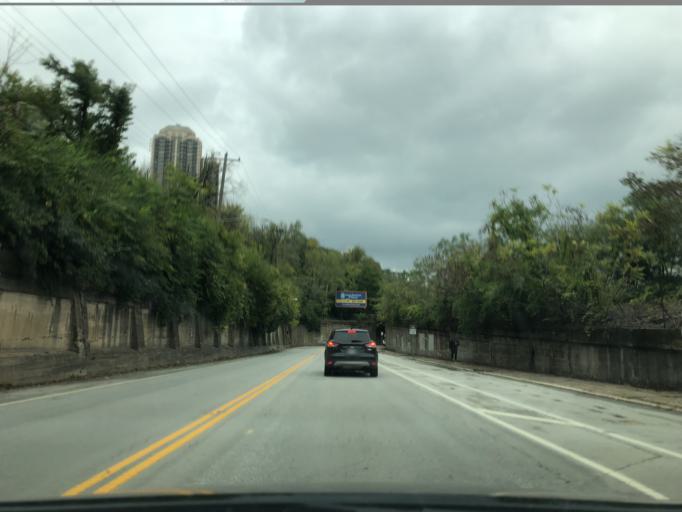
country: US
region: Kentucky
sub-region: Campbell County
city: Bellevue
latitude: 39.1159
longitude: -84.4856
